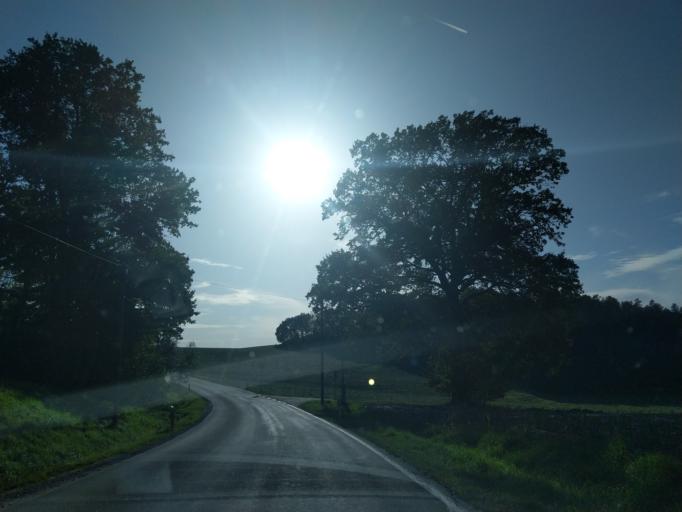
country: DE
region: Bavaria
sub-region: Lower Bavaria
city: Bernried
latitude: 48.9044
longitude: 12.8720
